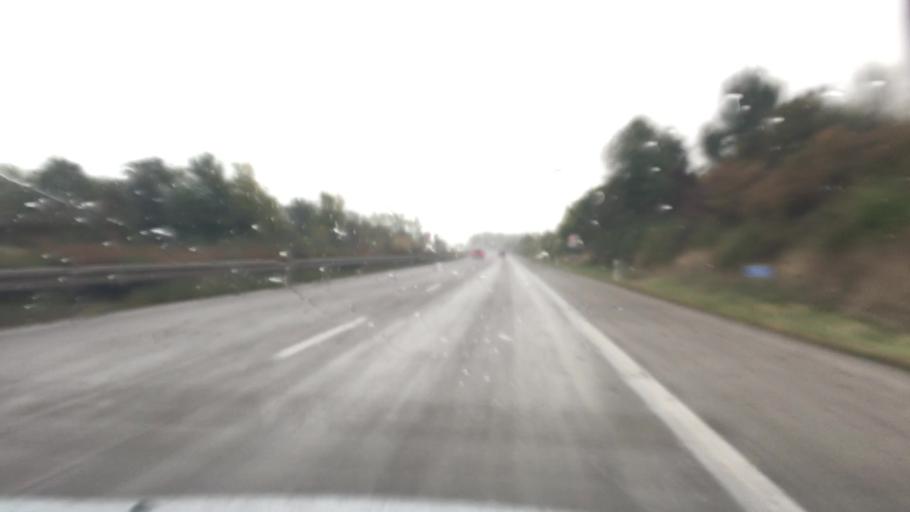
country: DE
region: Saxony-Anhalt
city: Biere
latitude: 51.9731
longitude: 11.6713
